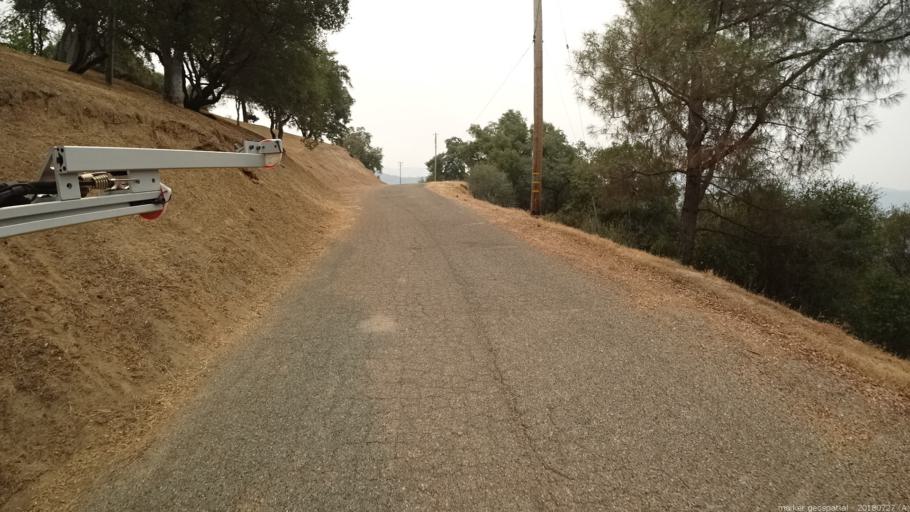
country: US
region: California
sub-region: Madera County
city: Oakhurst
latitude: 37.3394
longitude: -119.6243
